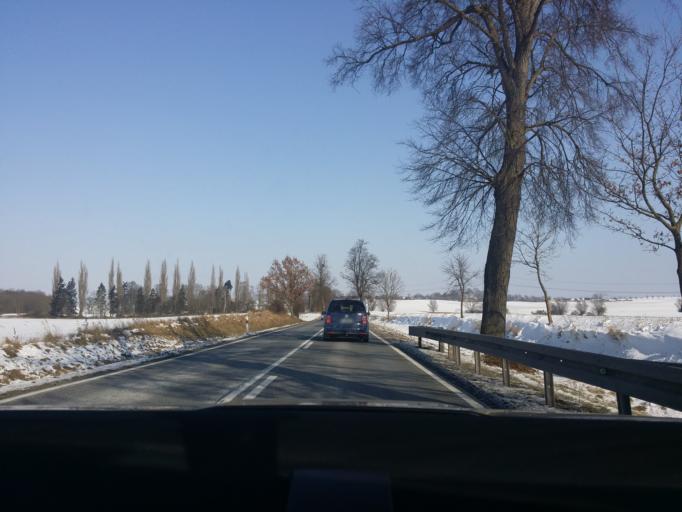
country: DE
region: Mecklenburg-Vorpommern
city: Penzlin
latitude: 53.5122
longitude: 13.1096
